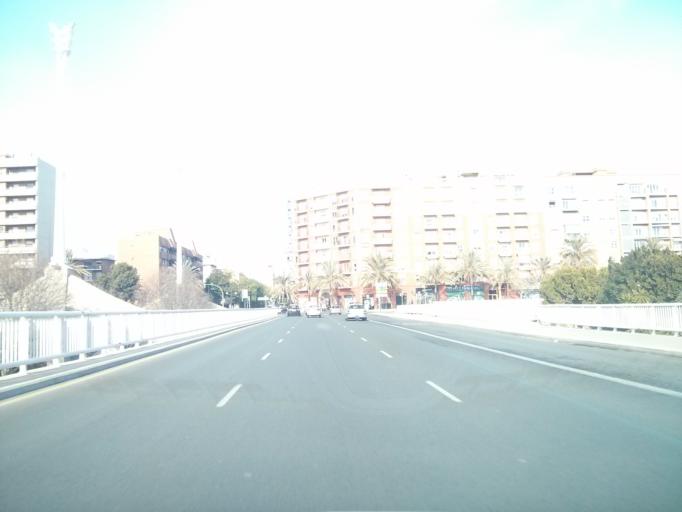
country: ES
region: Valencia
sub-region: Provincia de Valencia
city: Valencia
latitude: 39.4810
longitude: -0.3831
